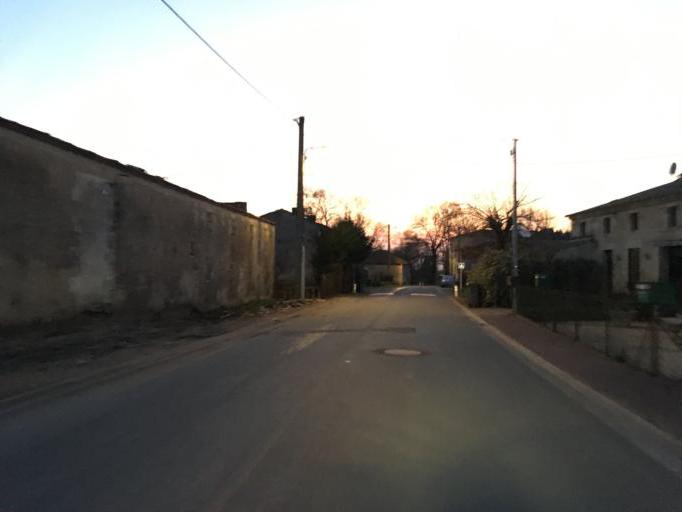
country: FR
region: Aquitaine
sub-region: Departement de la Gironde
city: Braud-et-Saint-Louis
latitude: 45.2459
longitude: -0.6380
